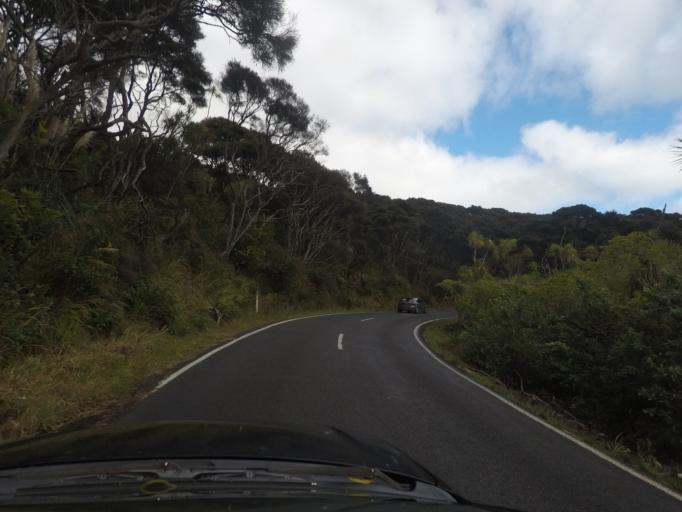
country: NZ
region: Auckland
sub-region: Auckland
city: Muriwai Beach
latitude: -36.8767
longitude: 174.4568
